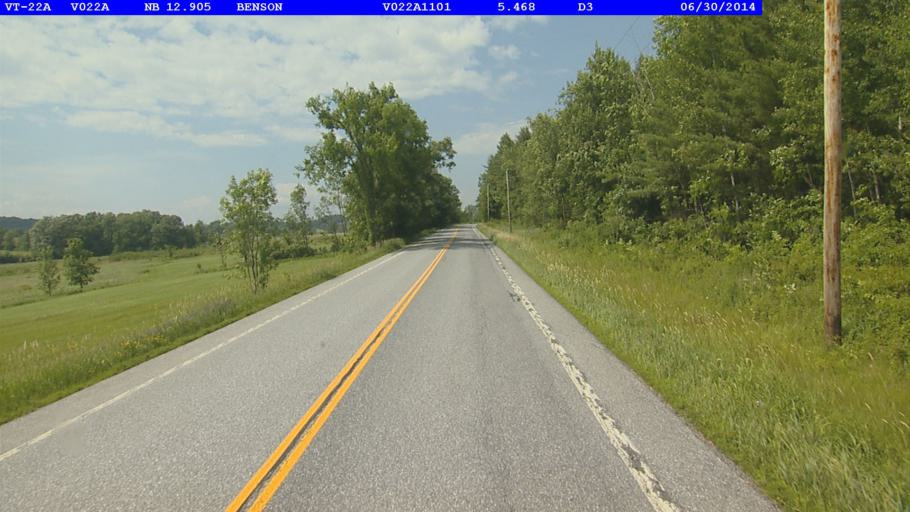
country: US
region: New York
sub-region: Essex County
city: Ticonderoga
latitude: 43.7463
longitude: -73.3075
